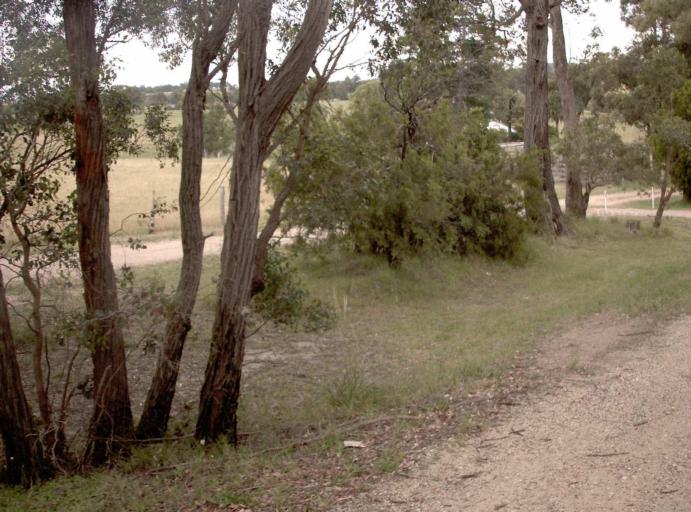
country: AU
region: Victoria
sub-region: East Gippsland
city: Bairnsdale
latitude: -37.7895
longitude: 147.6059
